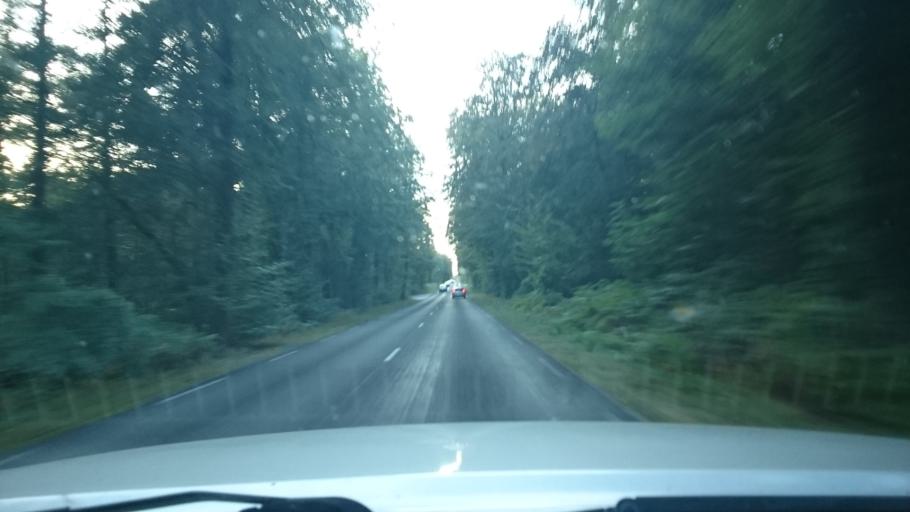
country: FR
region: Ile-de-France
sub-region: Departement de Seine-et-Marne
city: Samoreau
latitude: 48.4364
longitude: 2.7344
